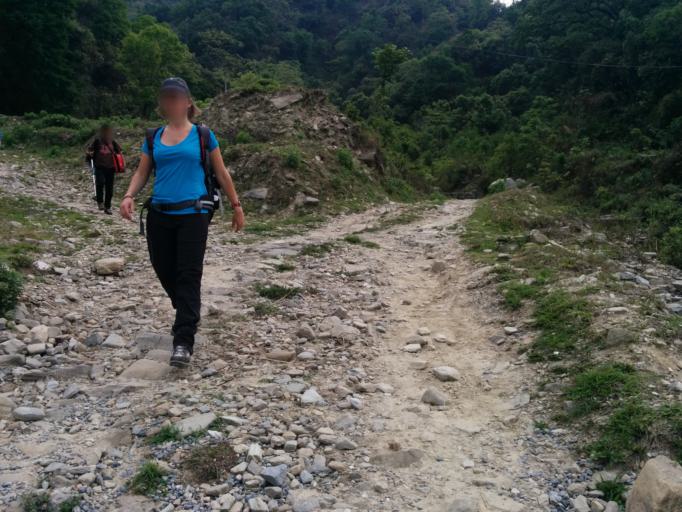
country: NP
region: Western Region
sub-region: Gandaki Zone
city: Pokhara
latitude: 28.2312
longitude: 83.9499
